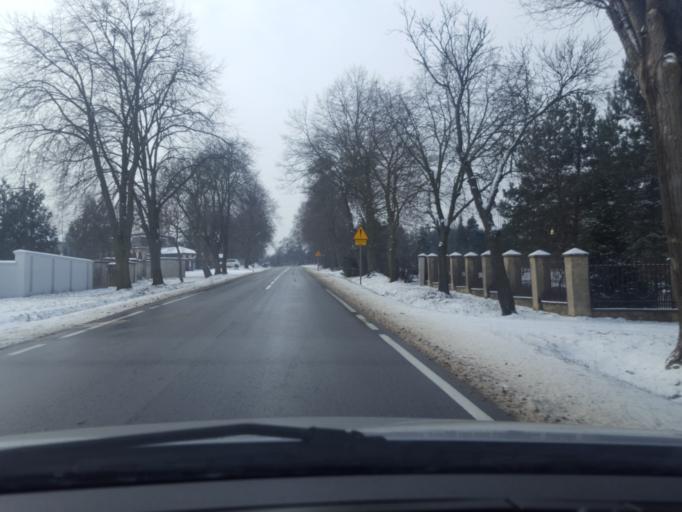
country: PL
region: Lodz Voivodeship
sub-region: Powiat brzezinski
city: Brzeziny
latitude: 51.8248
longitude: 19.7795
